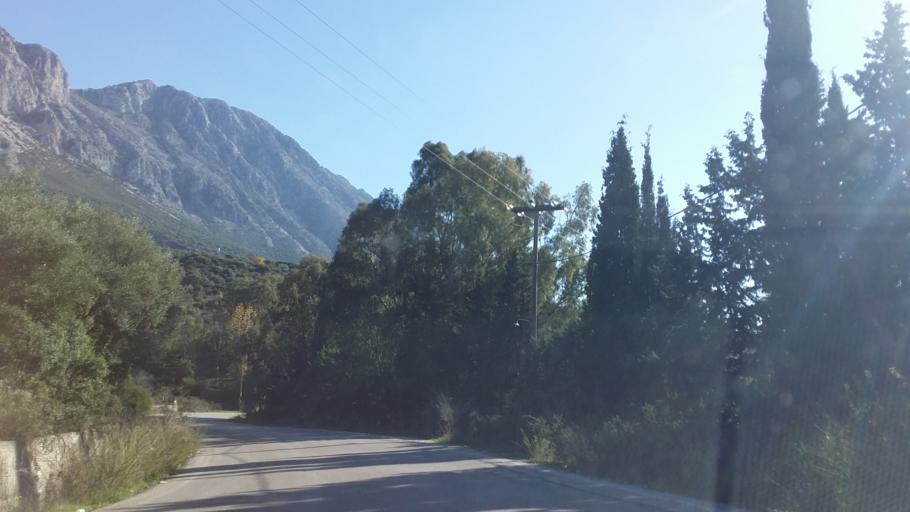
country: GR
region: West Greece
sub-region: Nomos Aitolias kai Akarnanias
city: Palairos
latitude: 38.7675
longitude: 20.8814
